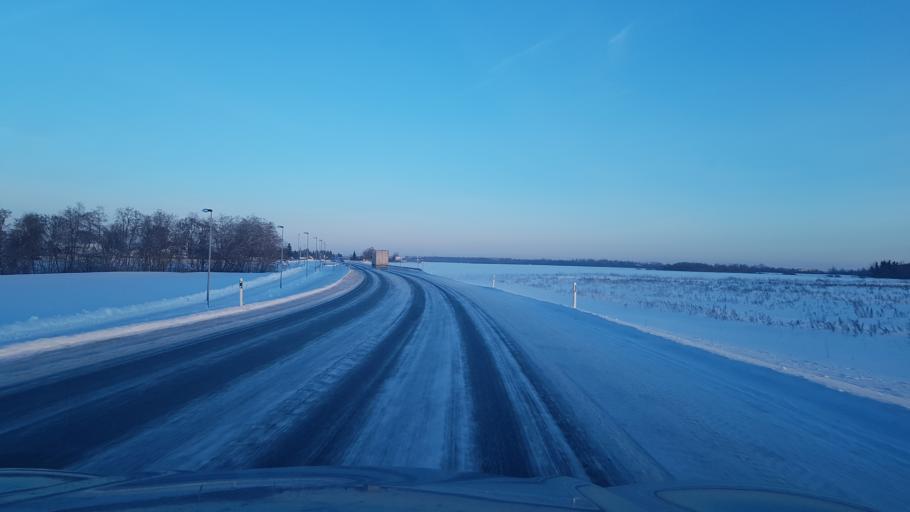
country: EE
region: Ida-Virumaa
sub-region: Narva-Joesuu linn
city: Narva-Joesuu
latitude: 59.3902
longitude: 28.0994
